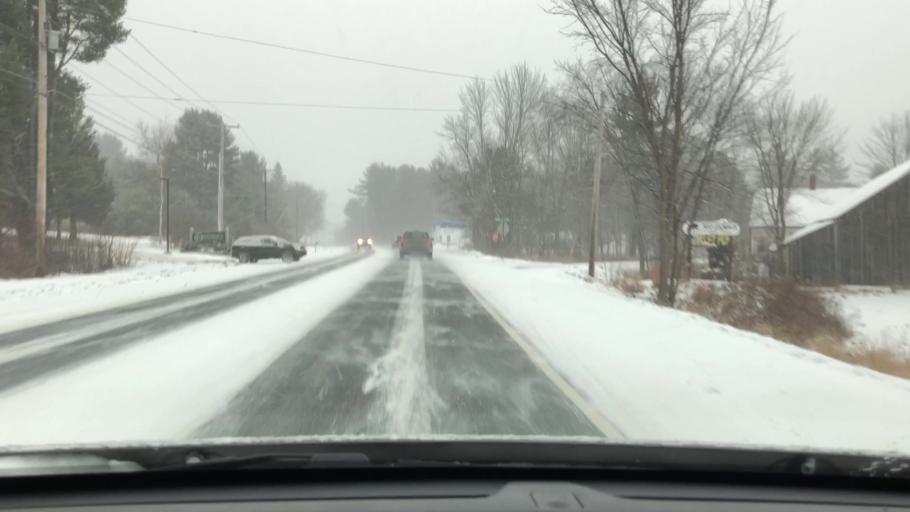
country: US
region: New Hampshire
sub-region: Strafford County
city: Lee
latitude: 43.1824
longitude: -70.9996
